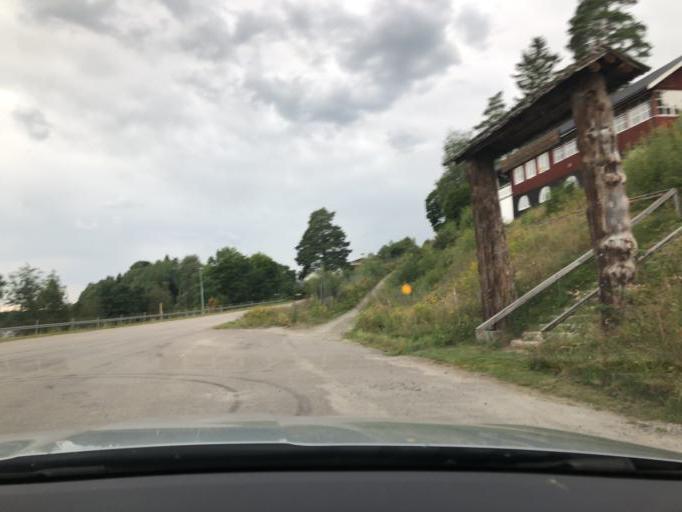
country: SE
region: Gaevleborg
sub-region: Ljusdals Kommun
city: Farila
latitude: 61.8056
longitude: 15.8487
